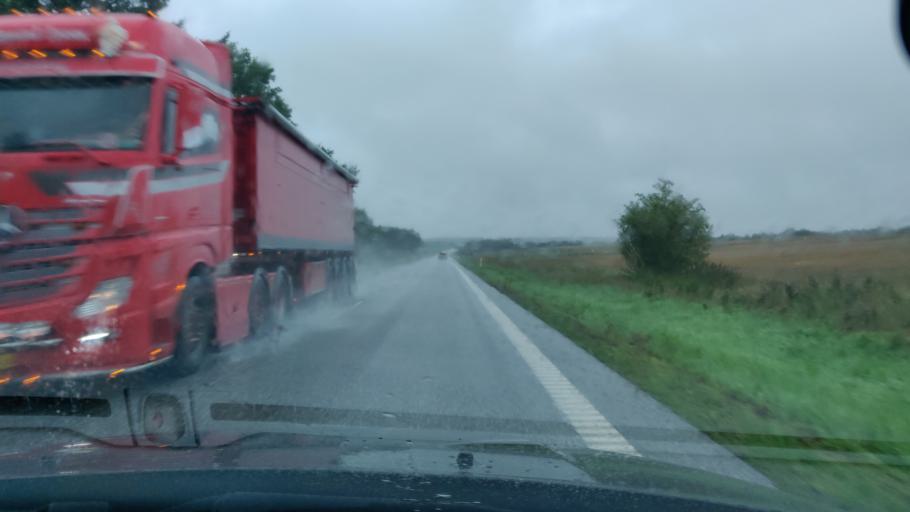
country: DK
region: North Denmark
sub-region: Thisted Kommune
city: Hurup
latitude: 56.8187
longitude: 8.4913
